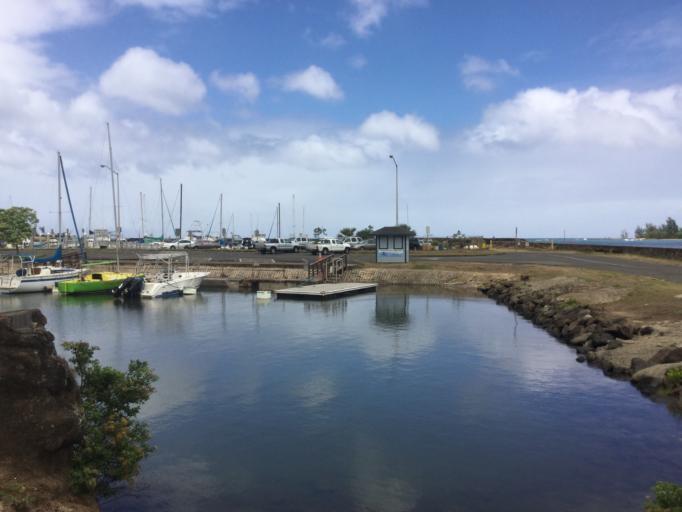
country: US
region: Hawaii
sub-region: Honolulu County
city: Hale'iwa
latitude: 21.5933
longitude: -158.1039
